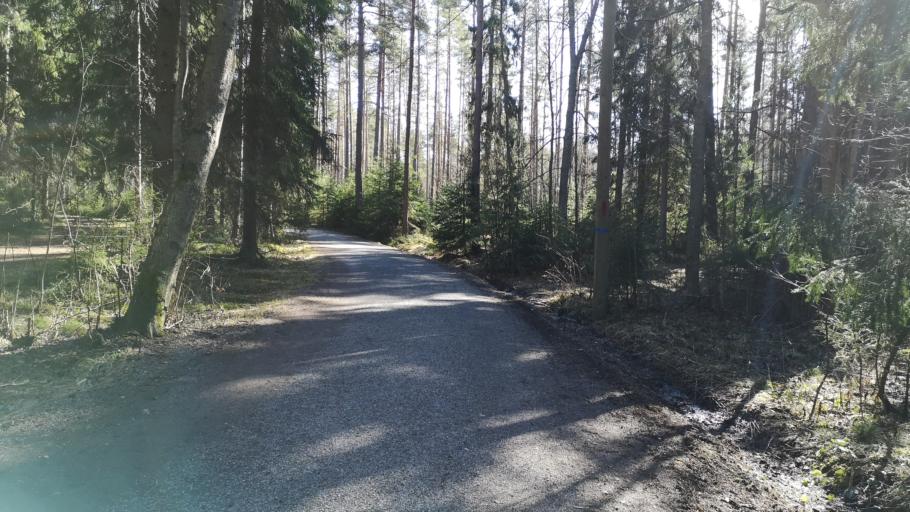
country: FI
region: Satakunta
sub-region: Pori
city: Pori
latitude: 61.4642
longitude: 21.7664
